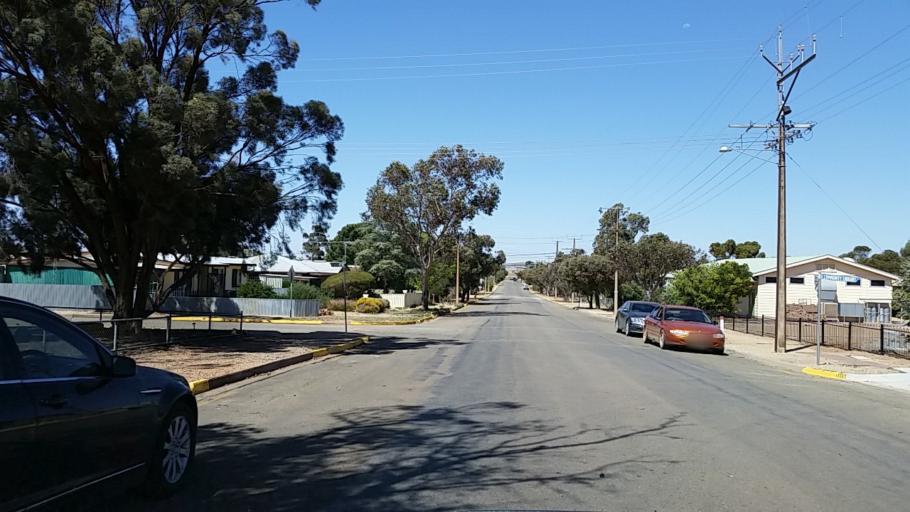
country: AU
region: South Australia
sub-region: Peterborough
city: Peterborough
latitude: -32.9780
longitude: 138.8359
